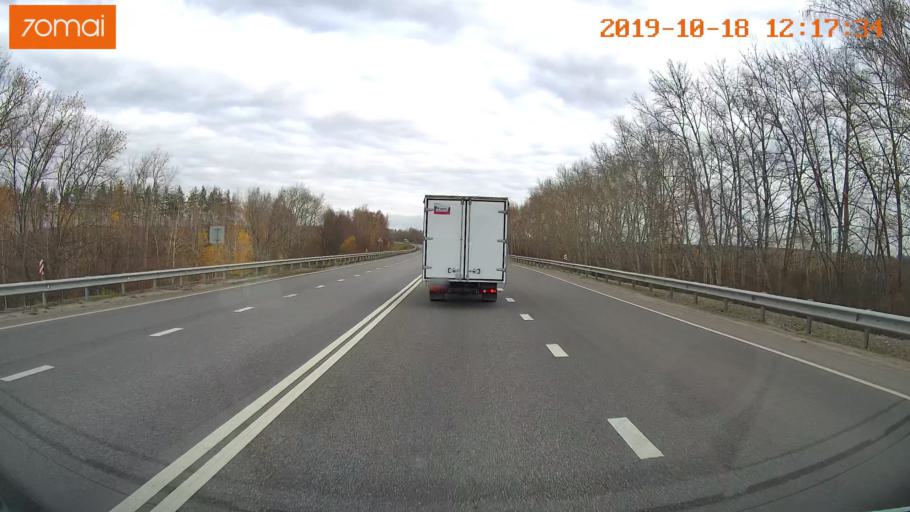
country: RU
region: Rjazan
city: Zakharovo
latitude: 54.4585
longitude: 39.4460
